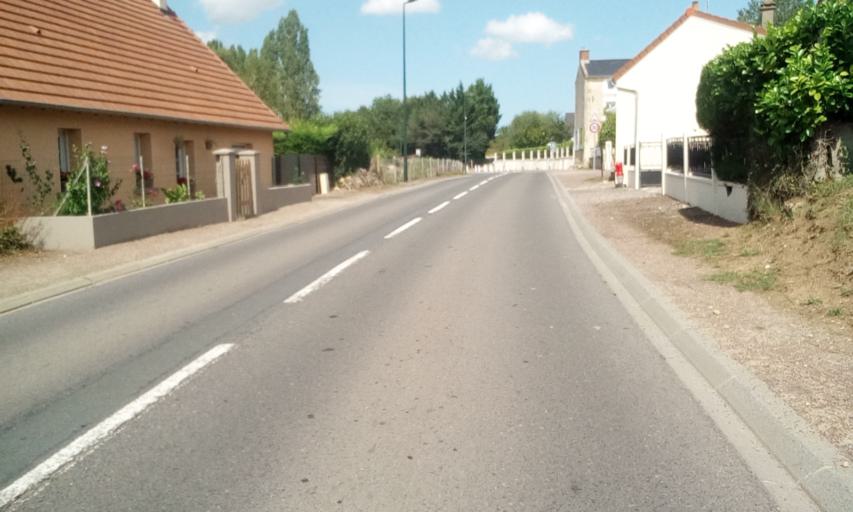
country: FR
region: Lower Normandy
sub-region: Departement du Calvados
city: Argences
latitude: 49.1447
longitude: -0.1638
